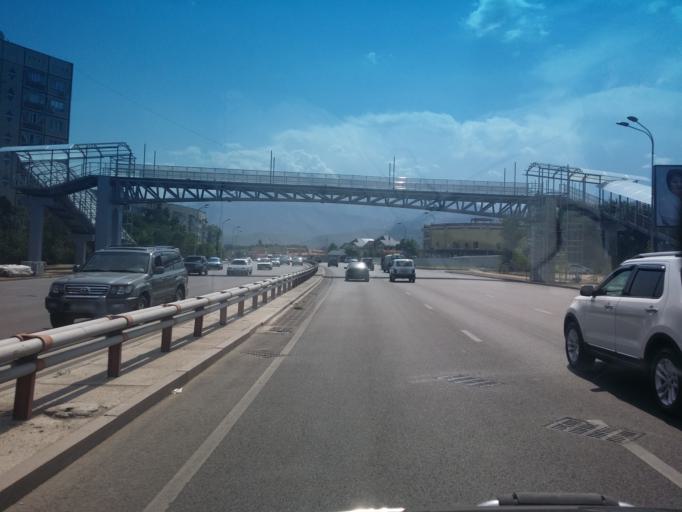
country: KZ
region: Almaty Qalasy
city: Almaty
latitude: 43.1973
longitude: 76.8718
